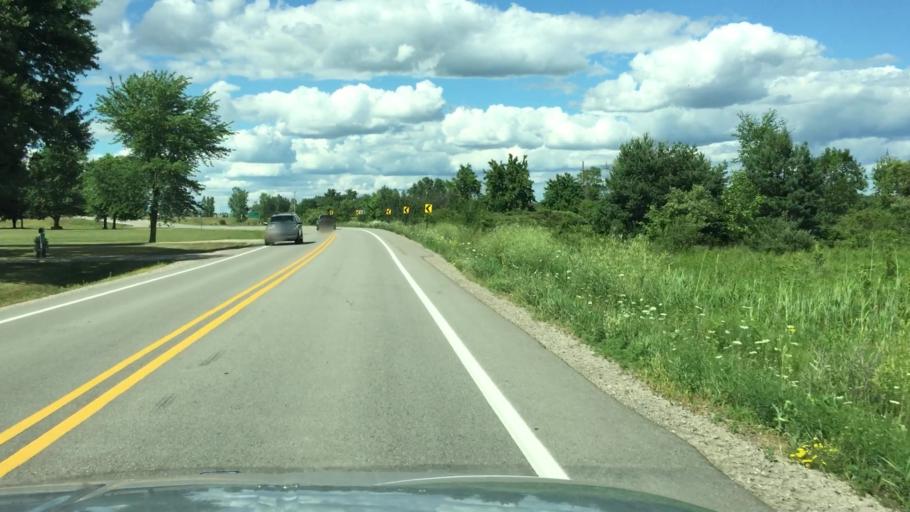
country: US
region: Michigan
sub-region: Saint Clair County
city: Capac
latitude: 42.9814
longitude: -82.9281
